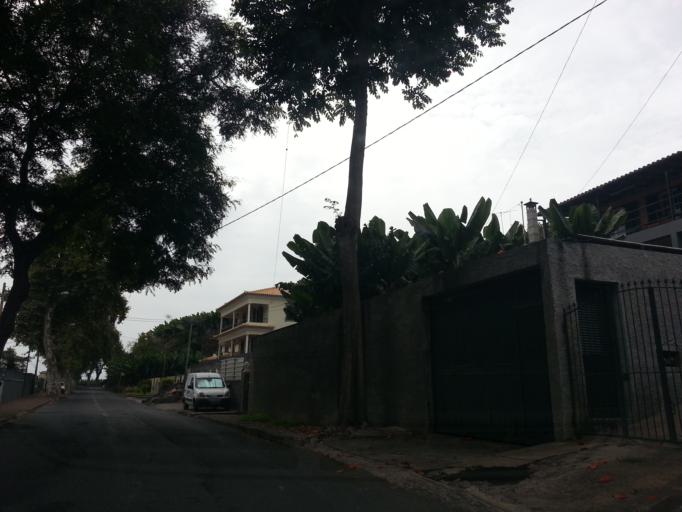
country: PT
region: Madeira
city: Camara de Lobos
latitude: 32.6458
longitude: -16.9613
